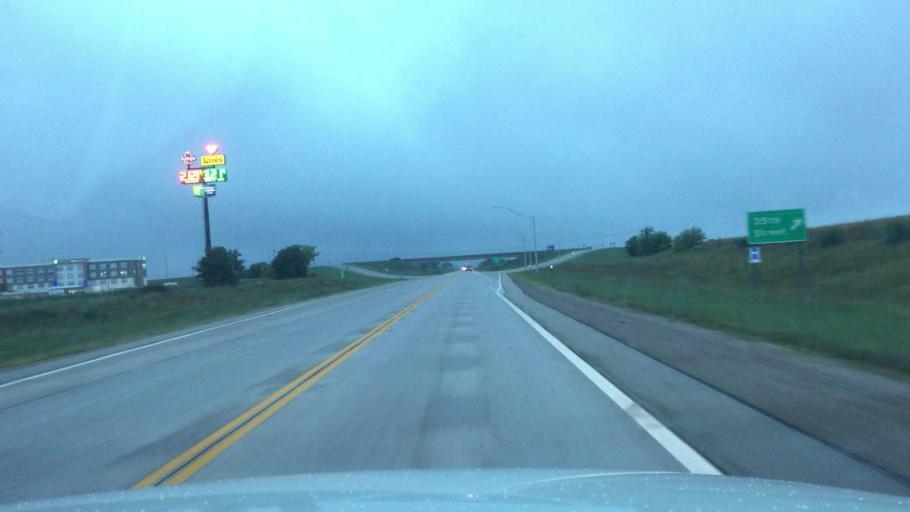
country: US
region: Kansas
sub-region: Neosho County
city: Chanute
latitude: 37.6499
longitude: -95.4797
